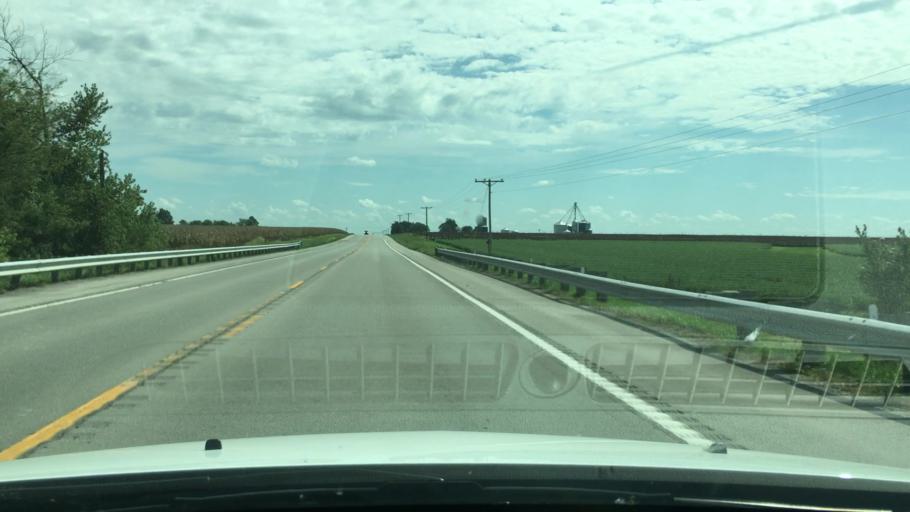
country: US
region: Missouri
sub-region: Audrain County
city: Mexico
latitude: 39.1638
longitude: -91.7494
